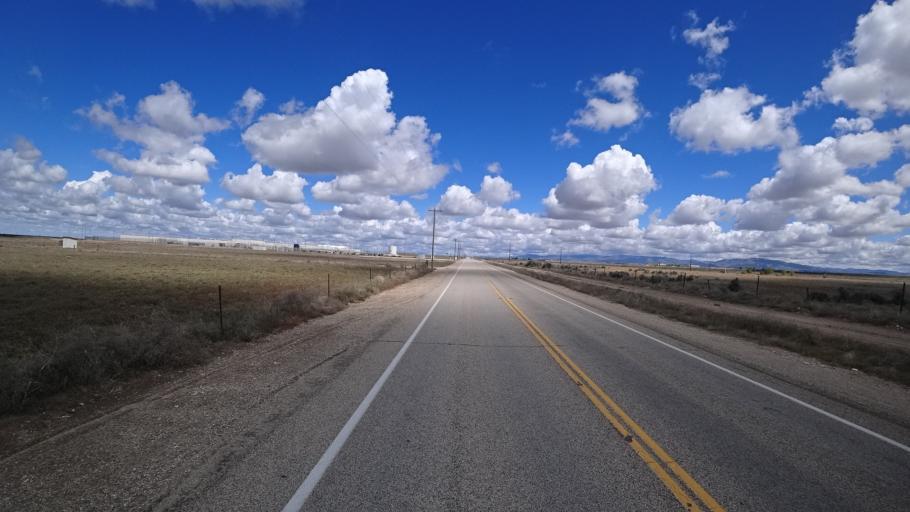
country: US
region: Idaho
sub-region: Ada County
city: Boise
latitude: 43.4671
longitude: -116.2348
